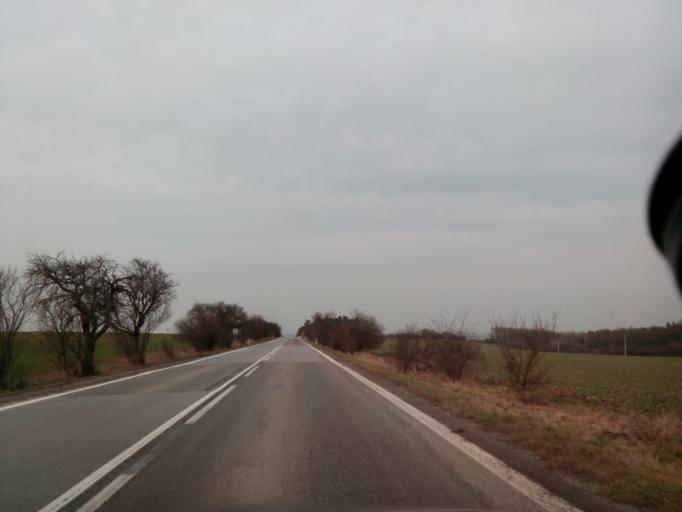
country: HU
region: Borsod-Abauj-Zemplen
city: Satoraljaujhely
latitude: 48.5094
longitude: 21.6561
